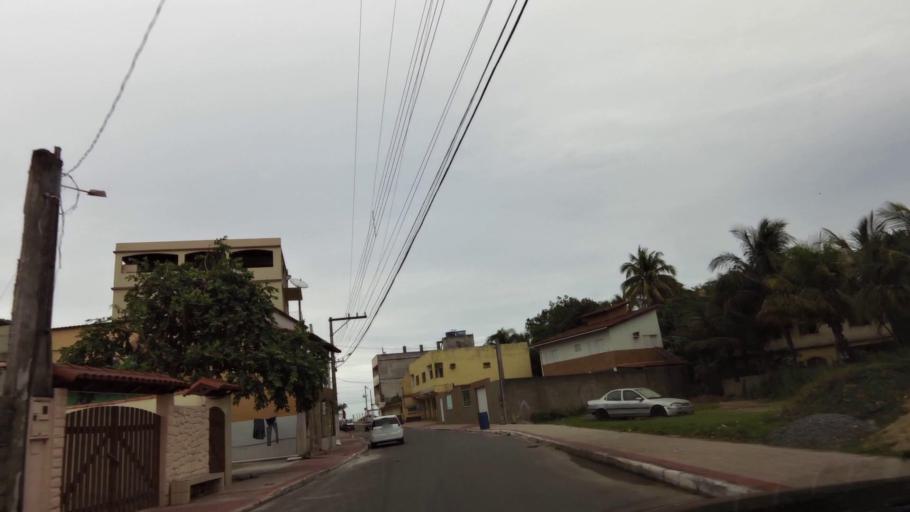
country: BR
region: Espirito Santo
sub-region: Piuma
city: Piuma
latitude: -20.8008
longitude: -40.5947
